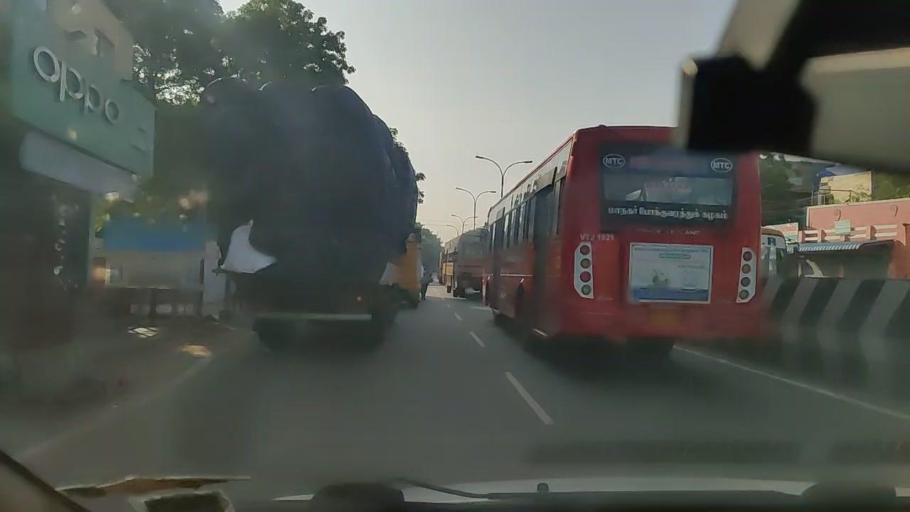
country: IN
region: Tamil Nadu
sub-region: Thiruvallur
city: Chinnasekkadu
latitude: 13.1265
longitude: 80.2450
